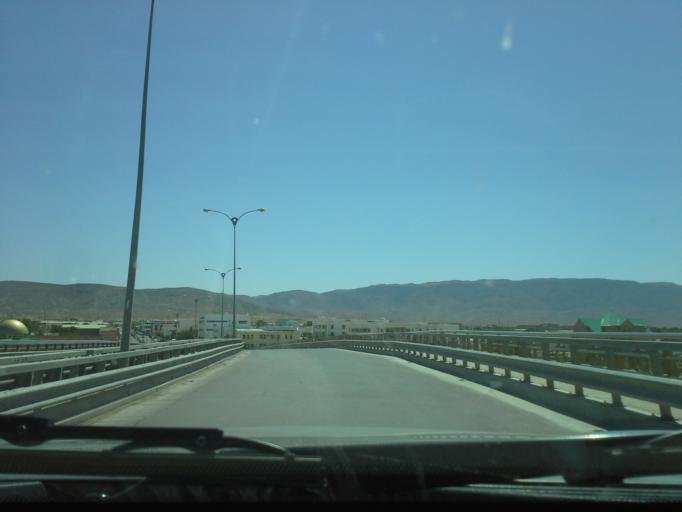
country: TM
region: Balkan
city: Serdar
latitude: 38.9792
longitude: 56.2780
